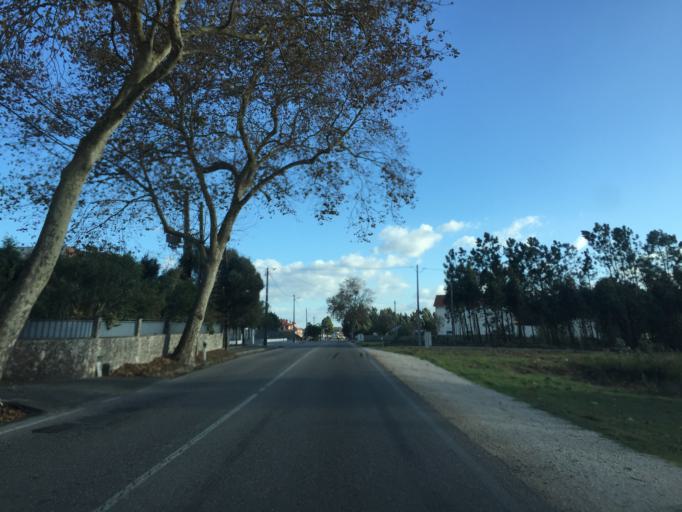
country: PT
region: Leiria
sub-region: Pombal
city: Lourical
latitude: 39.9635
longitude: -8.7902
